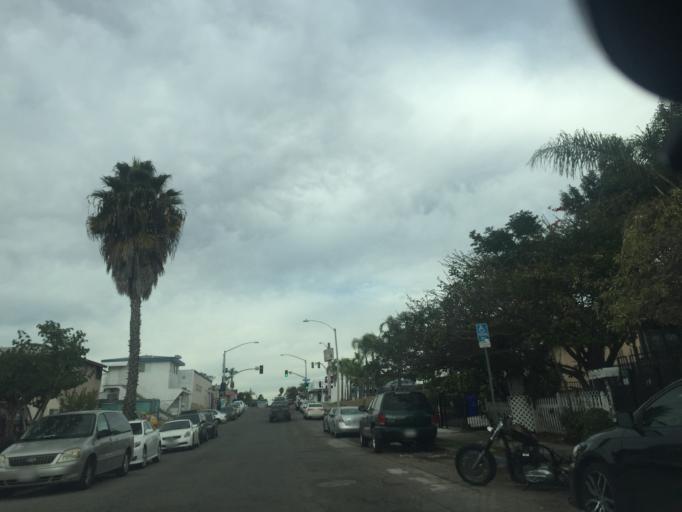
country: US
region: California
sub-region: San Diego County
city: Lemon Grove
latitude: 32.7556
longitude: -117.0879
